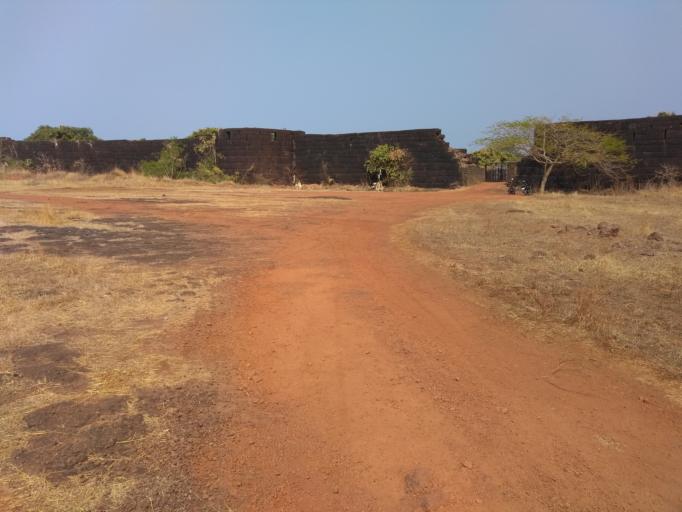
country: IN
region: Maharashtra
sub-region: Ratnagiri
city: Dabhol
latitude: 17.5702
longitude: 73.1522
